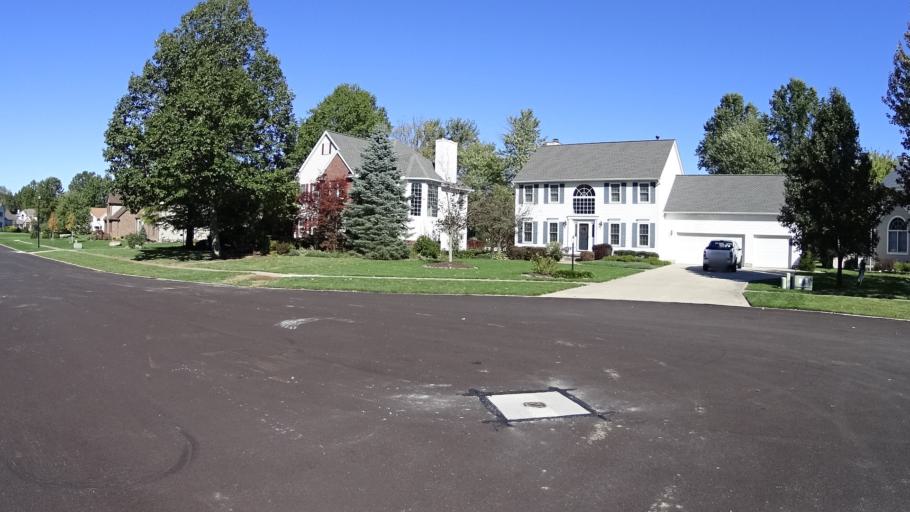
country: US
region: Ohio
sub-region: Lorain County
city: Amherst
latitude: 41.4027
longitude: -82.2469
